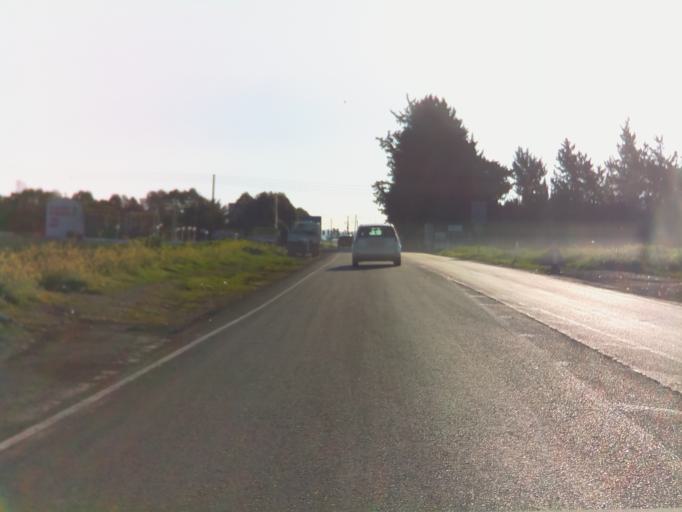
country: CY
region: Pafos
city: Paphos
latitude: 34.7283
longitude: 32.5132
